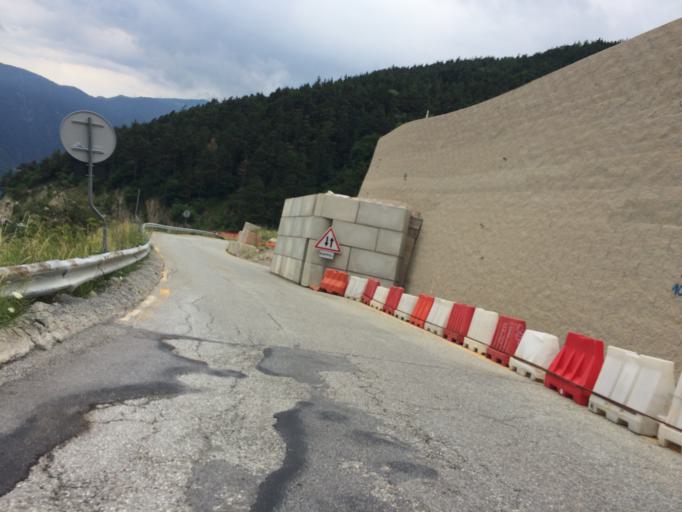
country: FR
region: Provence-Alpes-Cote d'Azur
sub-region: Departement des Alpes-Maritimes
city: Tende
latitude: 44.1378
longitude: 7.5680
